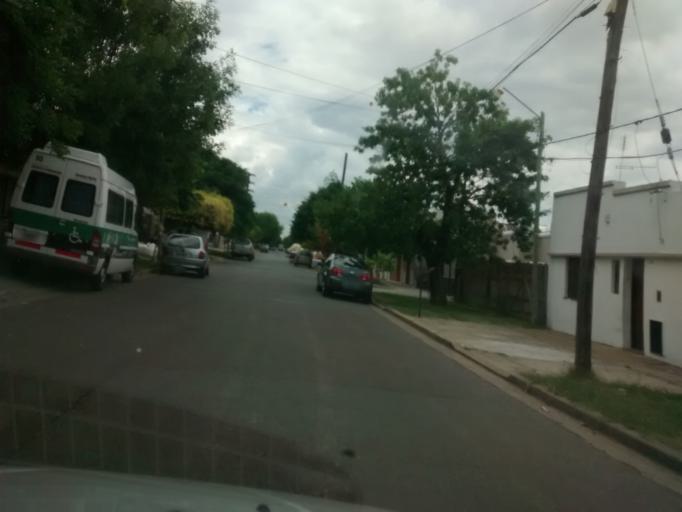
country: AR
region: Buenos Aires
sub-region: Partido de La Plata
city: La Plata
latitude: -34.9244
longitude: -57.9165
